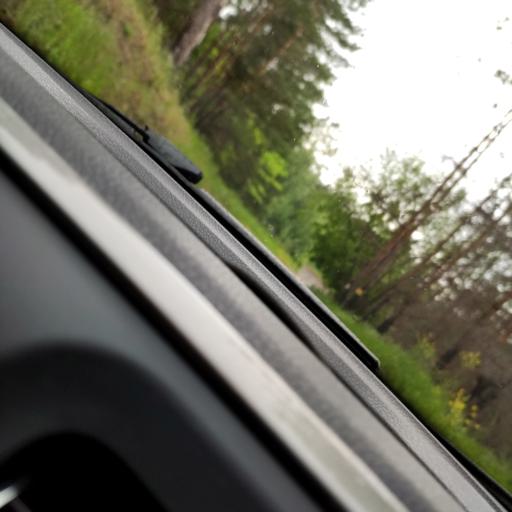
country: RU
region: Samara
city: Tol'yatti
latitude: 53.4722
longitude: 49.3718
